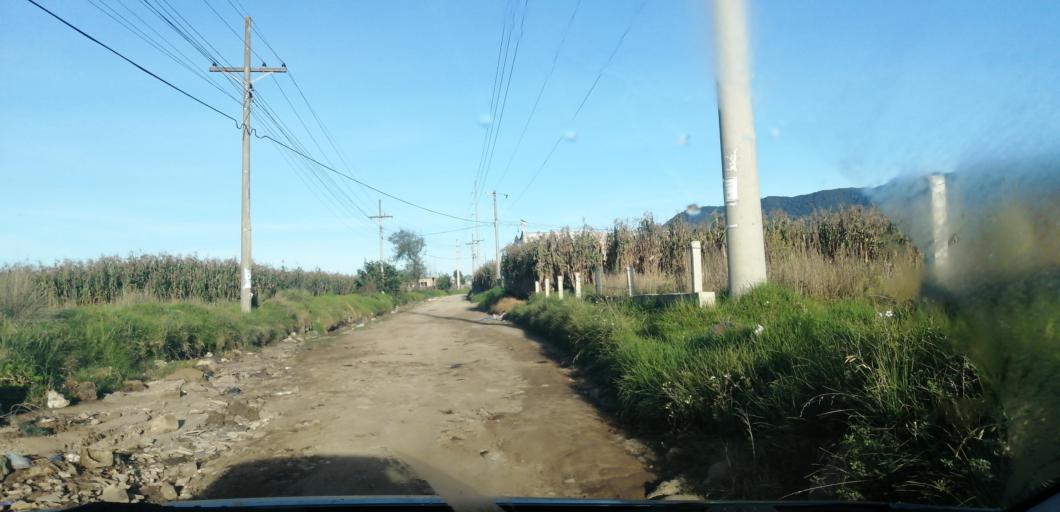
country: GT
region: Quetzaltenango
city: Olintepeque
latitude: 14.8678
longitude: -91.5288
